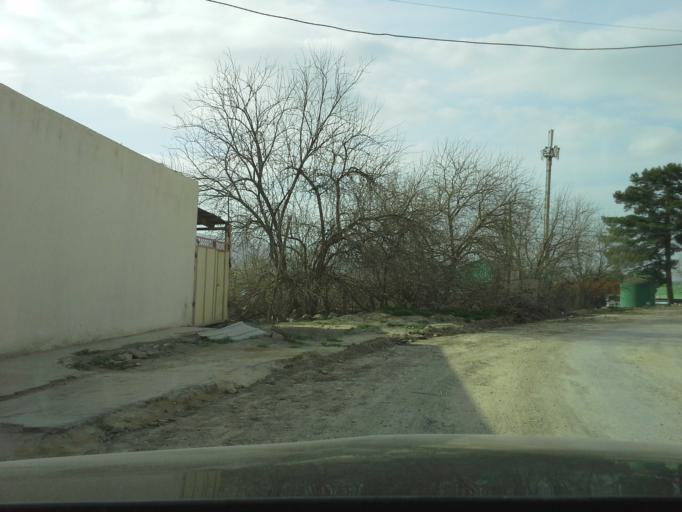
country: TM
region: Ahal
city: Abadan
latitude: 37.9557
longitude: 58.2066
